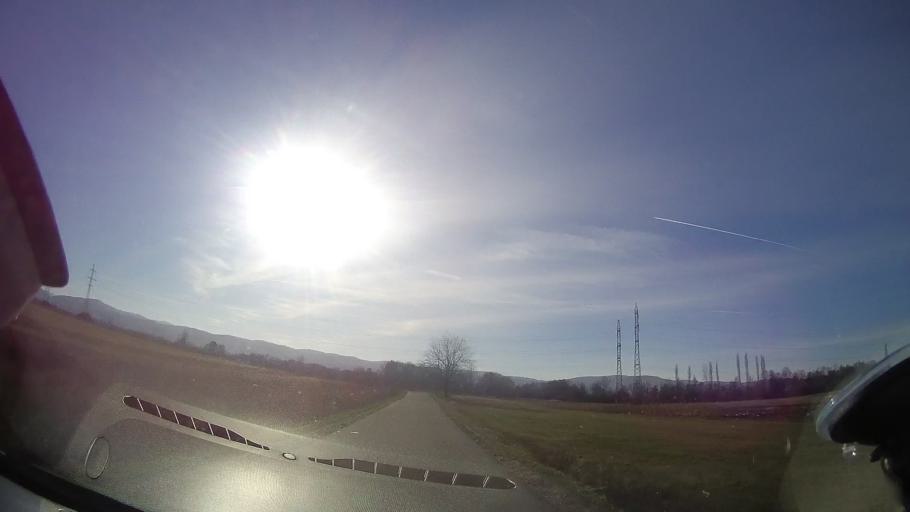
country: RO
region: Bihor
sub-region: Comuna Auseu
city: Grosi
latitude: 47.0278
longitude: 22.4822
